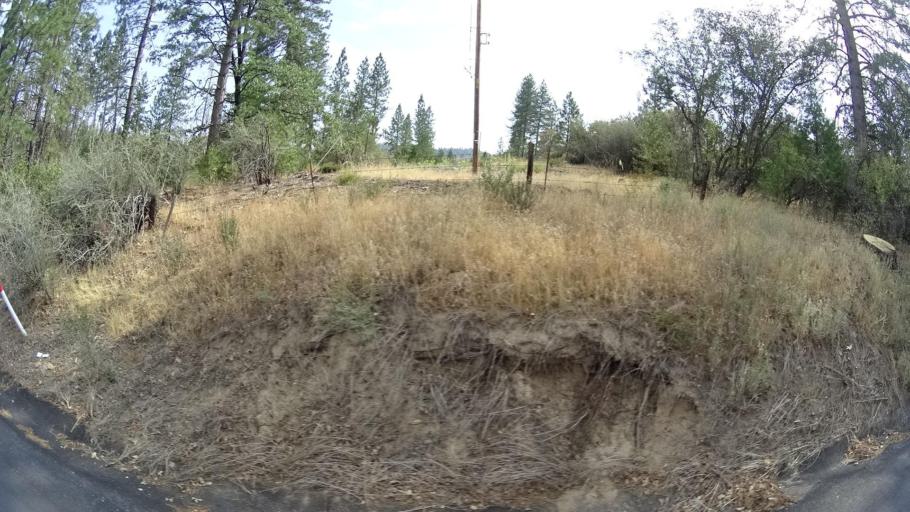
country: US
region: California
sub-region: Mariposa County
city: Midpines
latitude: 37.5164
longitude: -119.8348
